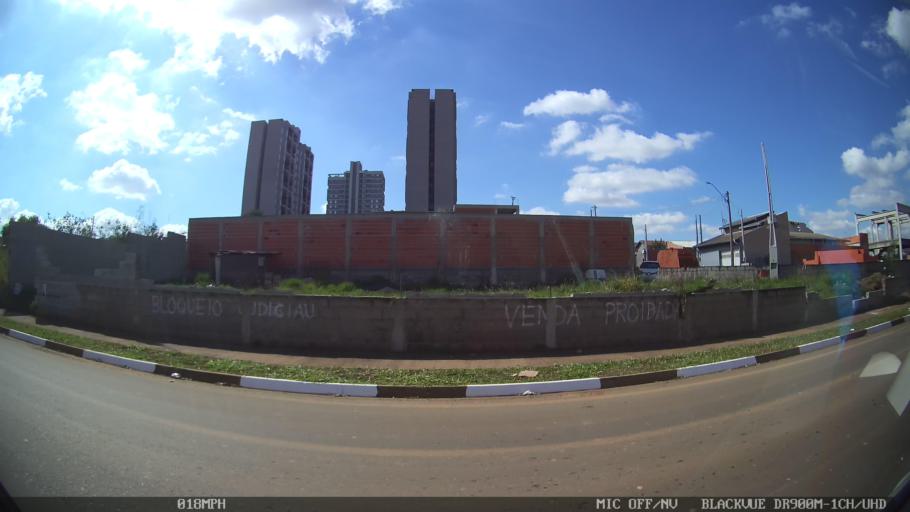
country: BR
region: Sao Paulo
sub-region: Hortolandia
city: Hortolandia
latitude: -22.8783
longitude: -47.2130
